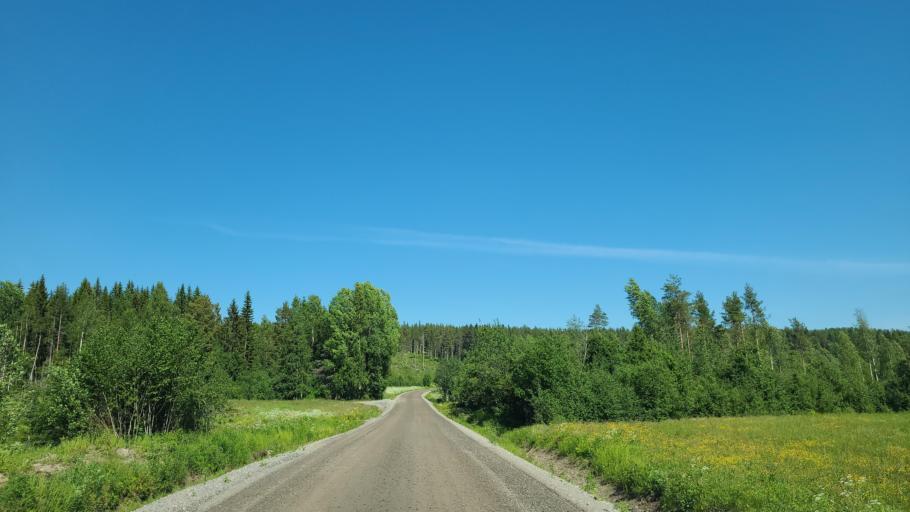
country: SE
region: Vaesterbotten
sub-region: Bjurholms Kommun
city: Bjurholm
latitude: 63.6747
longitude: 19.0384
